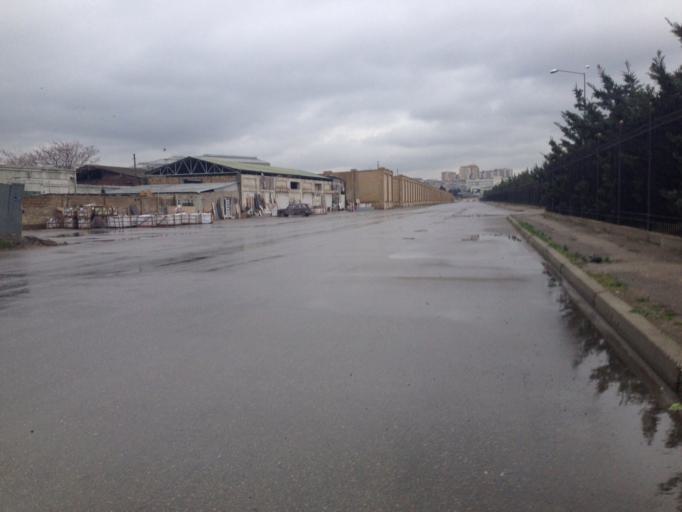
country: AZ
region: Baki
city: Baku
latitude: 40.4065
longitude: 49.8595
